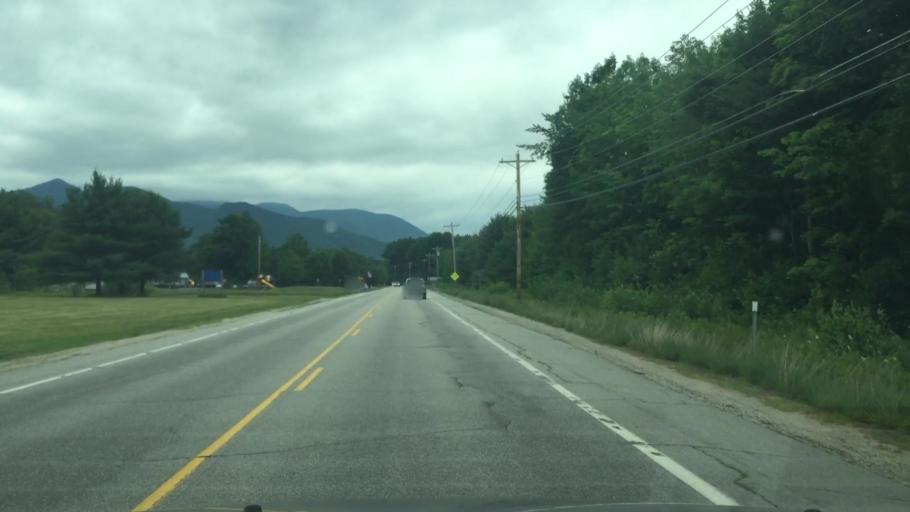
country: US
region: New Hampshire
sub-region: Carroll County
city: North Conway
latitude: 44.0809
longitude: -71.2503
